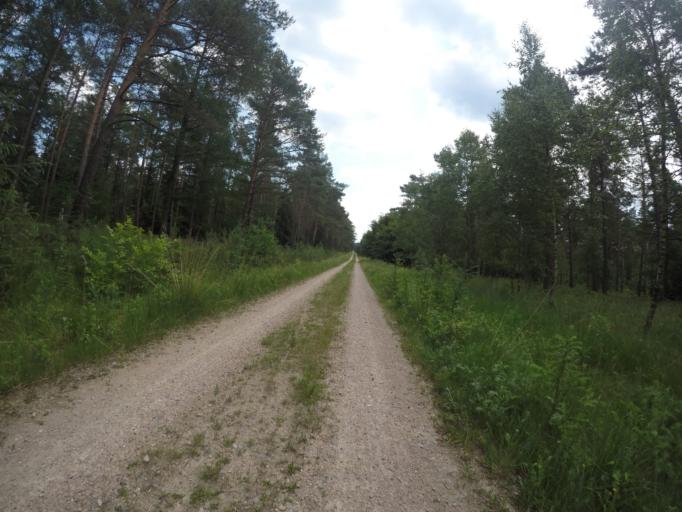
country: DE
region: Lower Saxony
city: Asendorf
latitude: 53.2509
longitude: 9.9518
